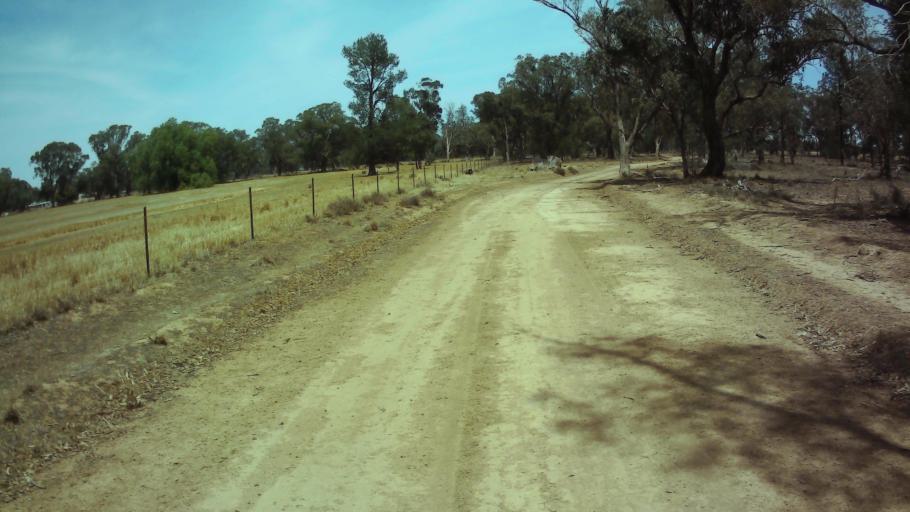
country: AU
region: New South Wales
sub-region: Weddin
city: Grenfell
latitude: -34.0333
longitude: 147.9296
